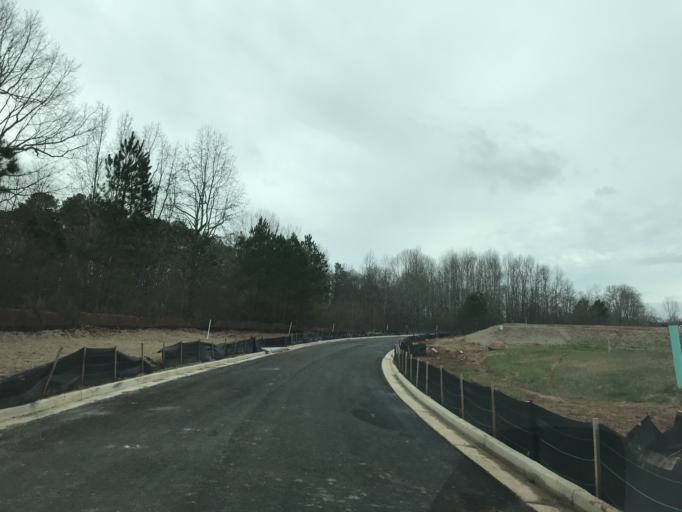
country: US
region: Georgia
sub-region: Cherokee County
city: Canton
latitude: 34.1955
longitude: -84.3982
